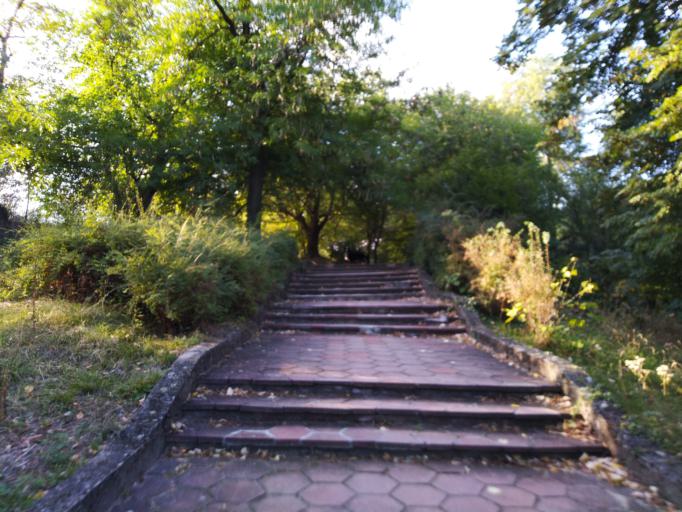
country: BG
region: Plovdiv
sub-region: Obshtina Khisarya
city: Khisarya
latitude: 42.4998
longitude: 24.7037
